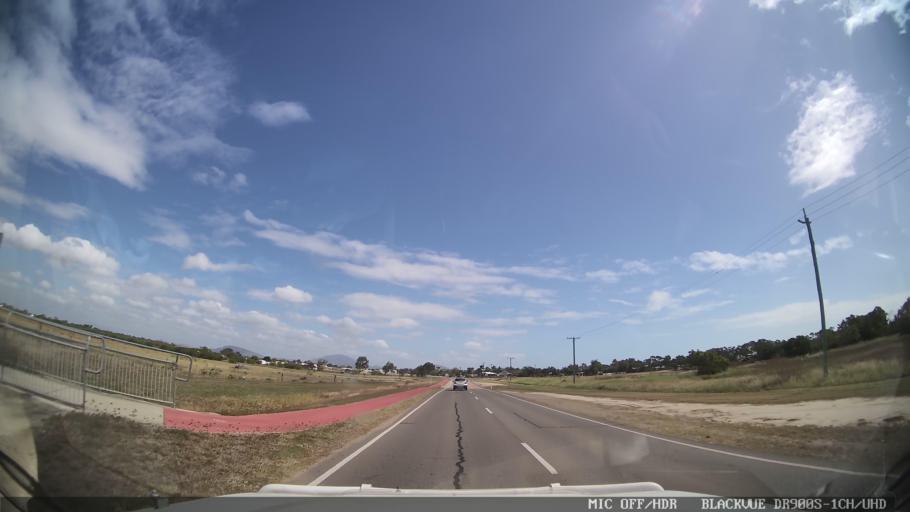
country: AU
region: Queensland
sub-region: Whitsunday
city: Bowen
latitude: -19.9994
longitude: 148.2303
